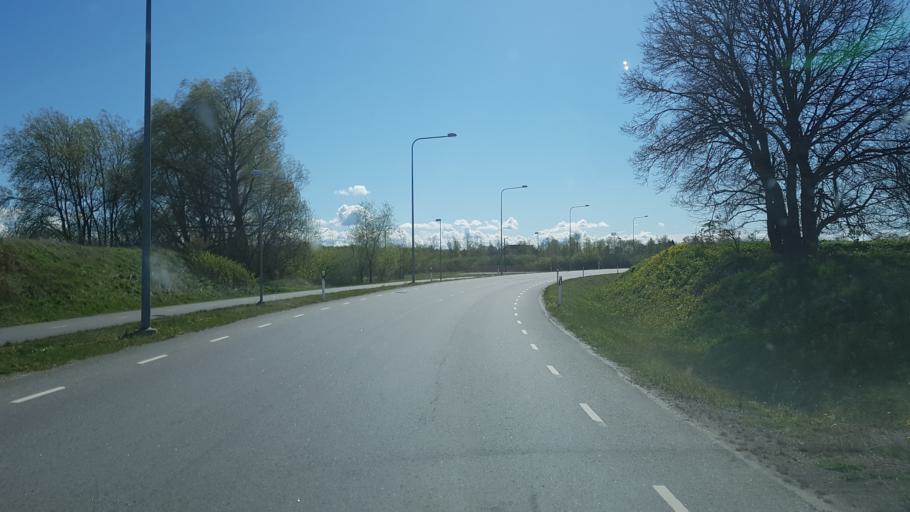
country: EE
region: Harju
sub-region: Joelaehtme vald
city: Loo
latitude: 59.4496
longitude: 24.9833
